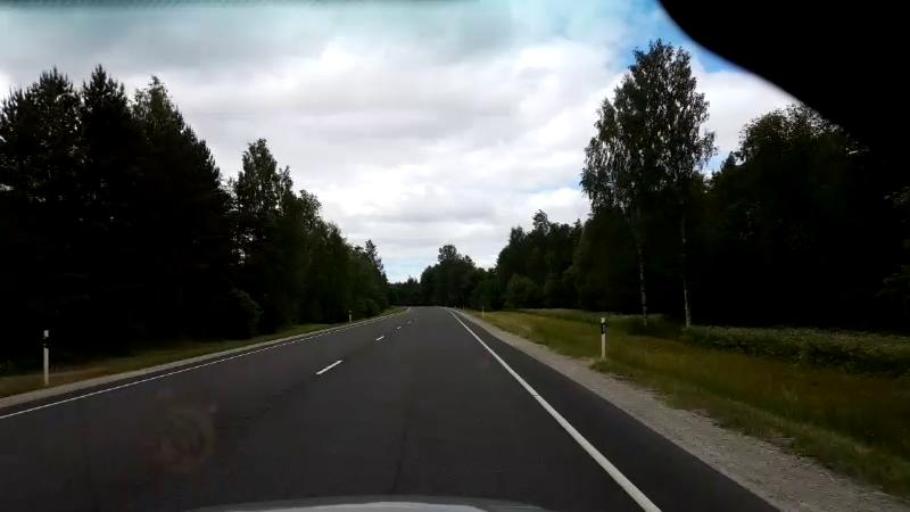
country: EE
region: Paernumaa
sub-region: Paernu linn
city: Parnu
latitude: 58.2525
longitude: 24.5262
